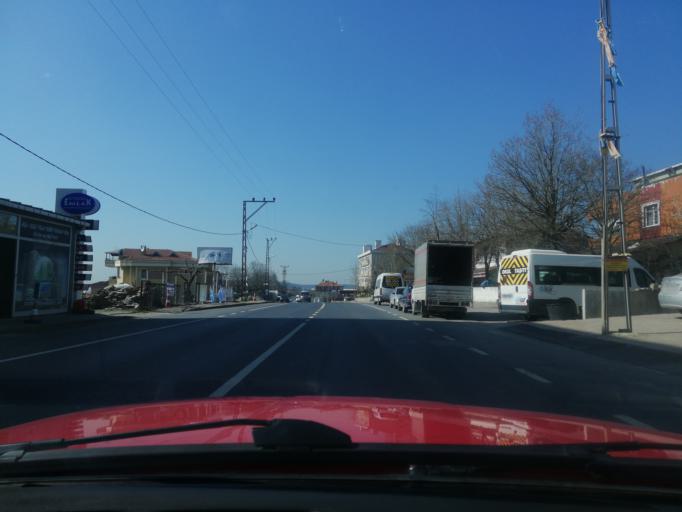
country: TR
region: Istanbul
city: Umraniye
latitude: 41.0686
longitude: 29.1643
